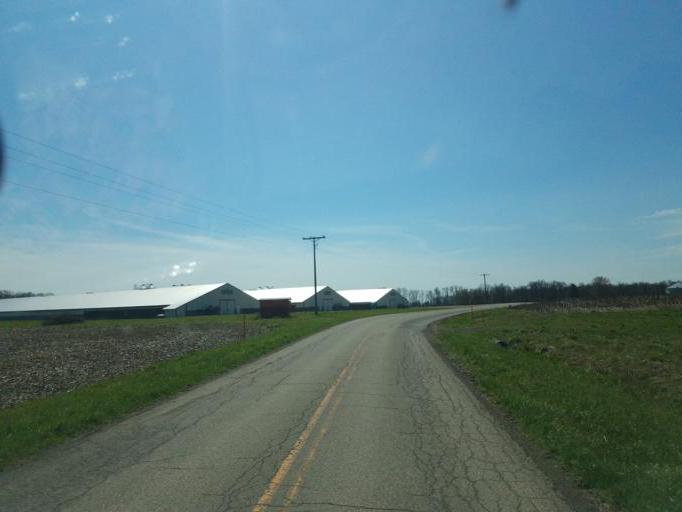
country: US
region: Ohio
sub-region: Knox County
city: Oak Hill
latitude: 40.3259
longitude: -82.2708
